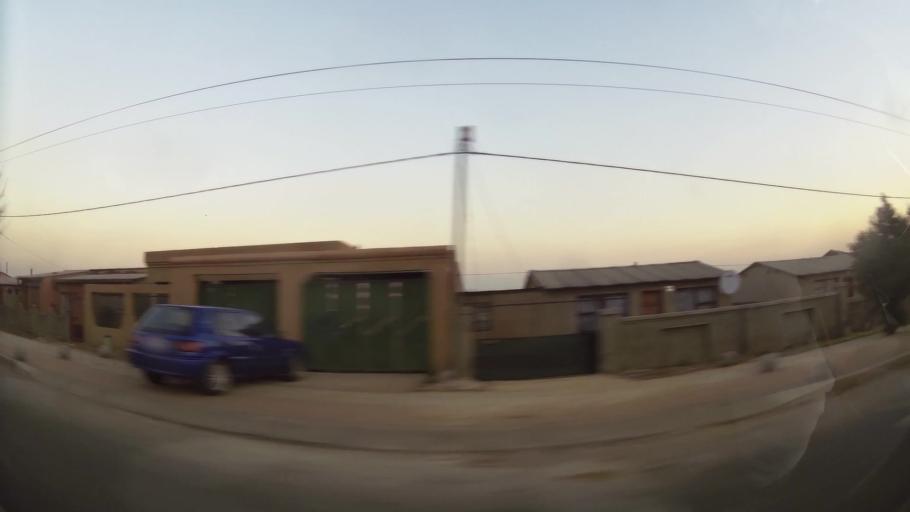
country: ZA
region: Gauteng
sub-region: Ekurhuleni Metropolitan Municipality
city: Nigel
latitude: -26.3750
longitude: 28.4065
